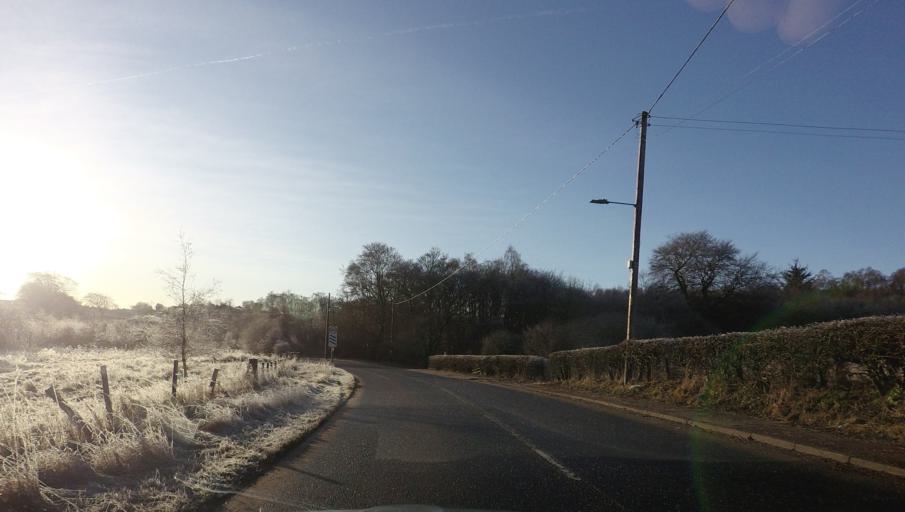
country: GB
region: Scotland
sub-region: North Lanarkshire
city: Shotts
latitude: 55.8049
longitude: -3.8404
